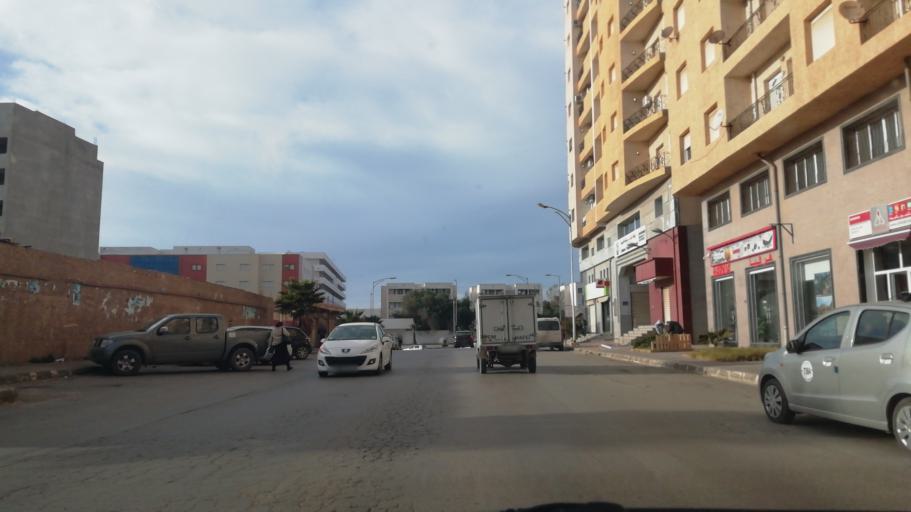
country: DZ
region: Oran
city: Bir el Djir
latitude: 35.7375
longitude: -0.5712
